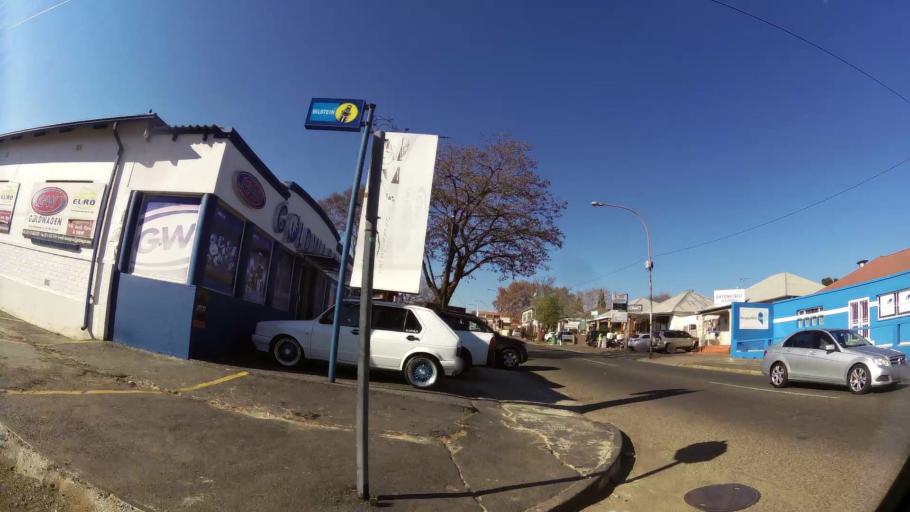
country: ZA
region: Gauteng
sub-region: City of Johannesburg Metropolitan Municipality
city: Johannesburg
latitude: -26.1869
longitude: 28.1071
